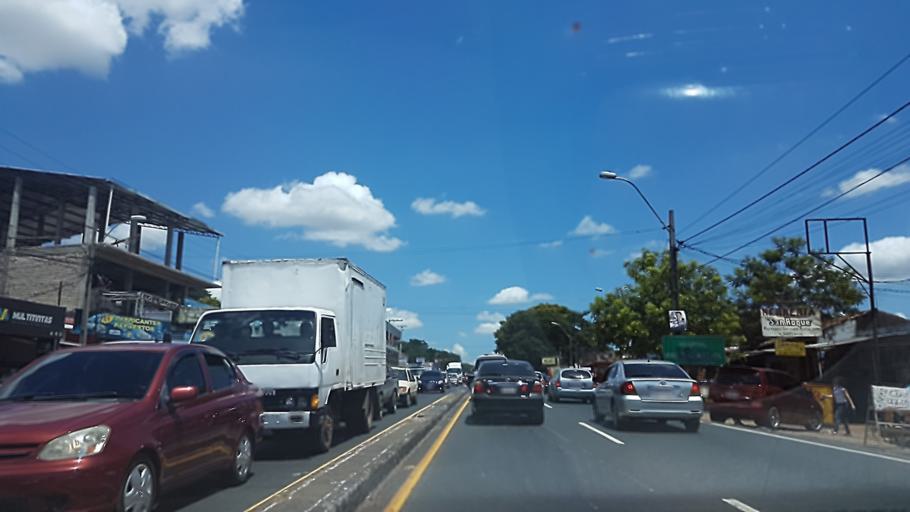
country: PY
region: Central
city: Capiata
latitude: -25.3521
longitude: -57.4449
